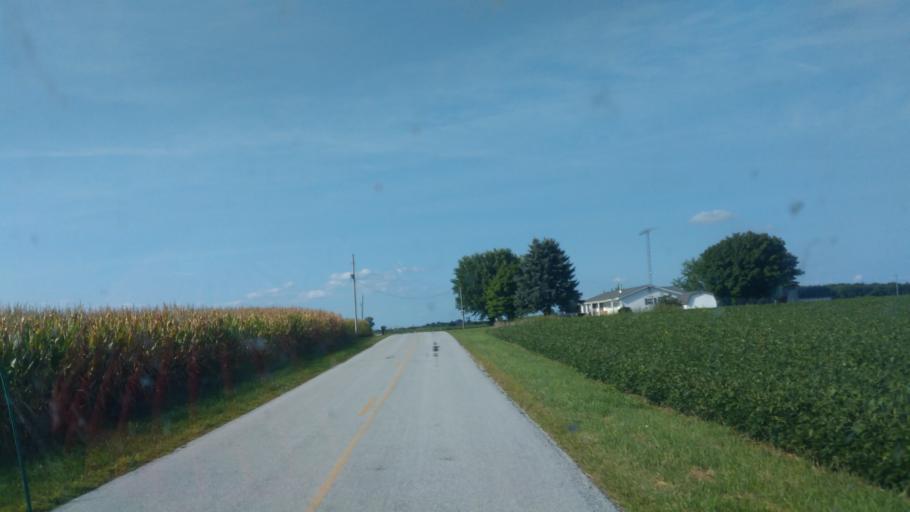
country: US
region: Ohio
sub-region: Hardin County
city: Kenton
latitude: 40.7225
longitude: -83.5725
